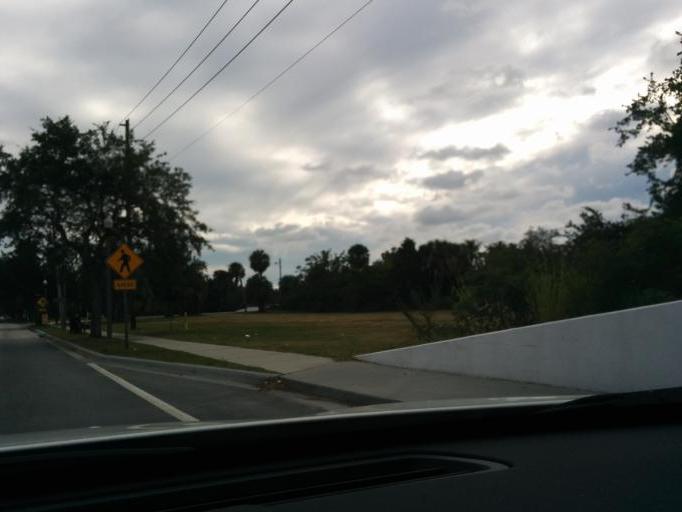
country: US
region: Florida
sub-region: Pinellas County
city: Saint Petersburg
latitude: 27.7531
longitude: -82.6386
